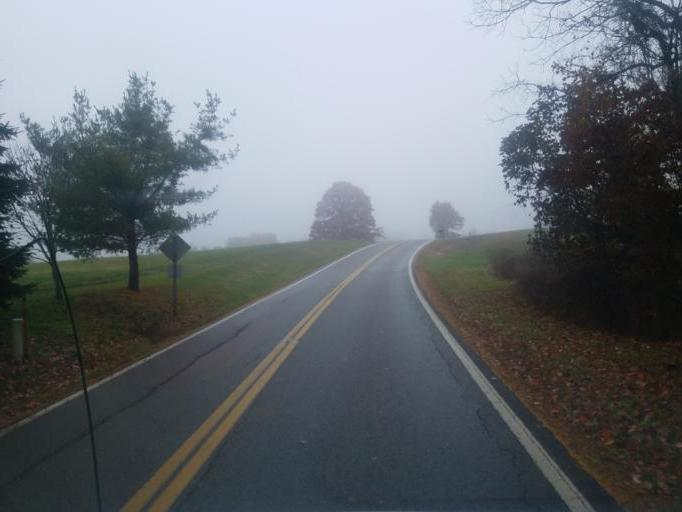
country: US
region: Ohio
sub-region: Morgan County
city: McConnelsville
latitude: 39.5249
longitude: -81.7934
